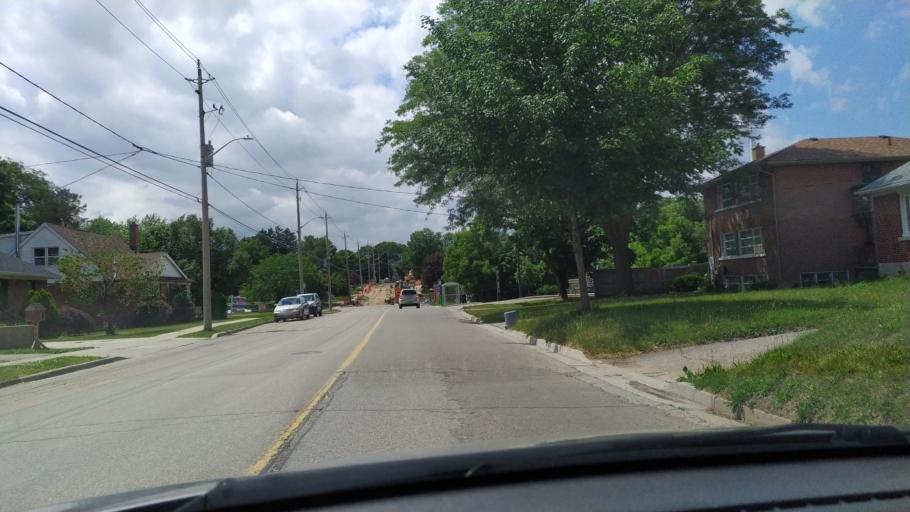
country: CA
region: Ontario
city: Kitchener
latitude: 43.4350
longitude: -80.4821
